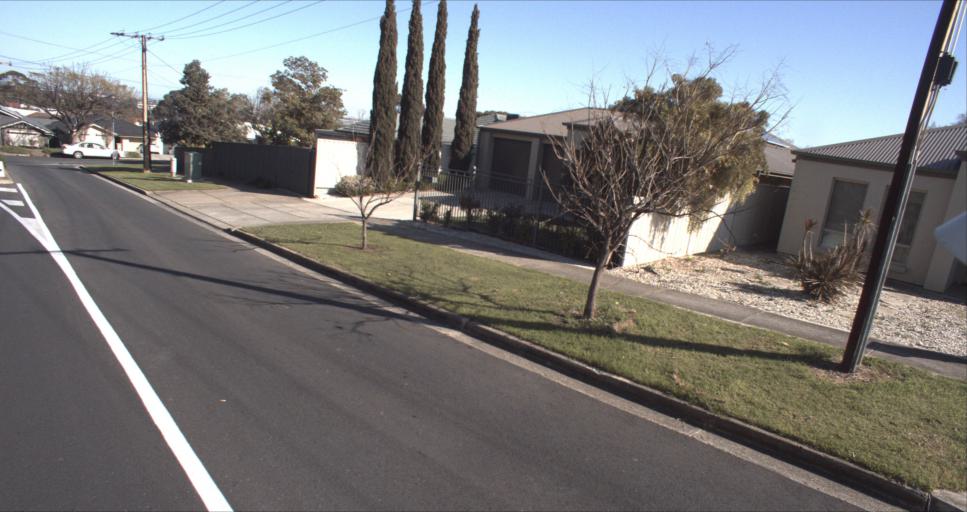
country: AU
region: South Australia
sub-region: Port Adelaide Enfield
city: Enfield
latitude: -34.8561
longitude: 138.6068
